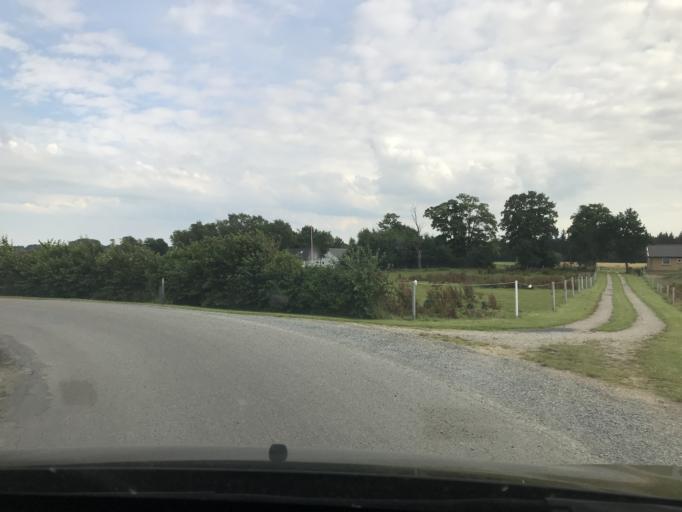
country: DK
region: South Denmark
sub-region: Vejle Kommune
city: Jelling
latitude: 55.8035
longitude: 9.3986
